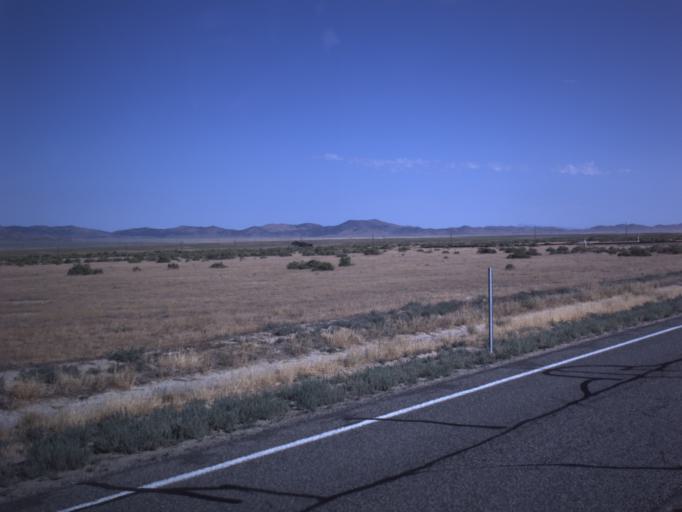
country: US
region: Utah
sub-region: Beaver County
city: Milford
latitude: 38.4929
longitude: -112.9911
